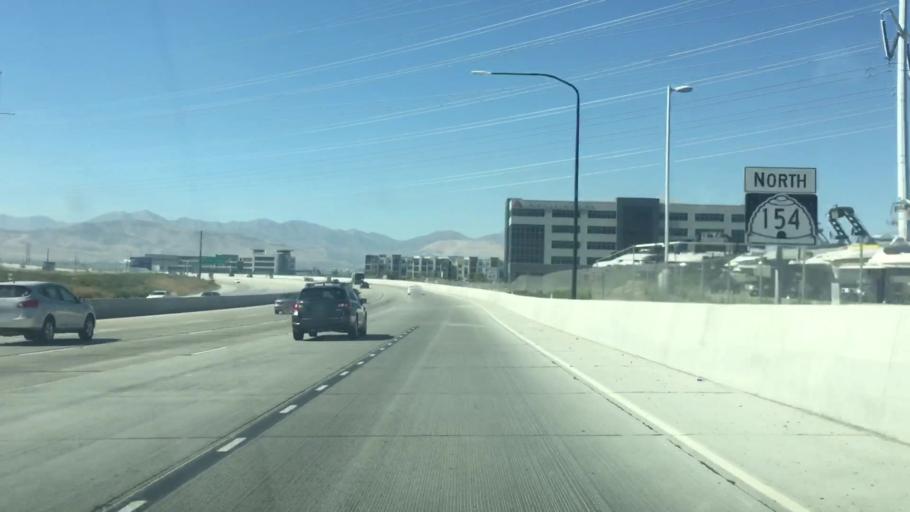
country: US
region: Utah
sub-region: Salt Lake County
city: Draper
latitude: 40.5045
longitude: -111.8984
